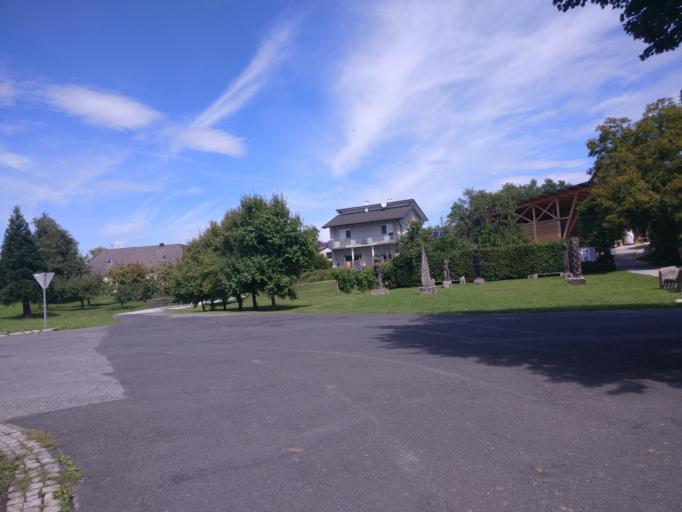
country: AT
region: Styria
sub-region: Politischer Bezirk Hartberg-Fuerstenfeld
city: Hartl
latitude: 47.1485
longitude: 15.8942
